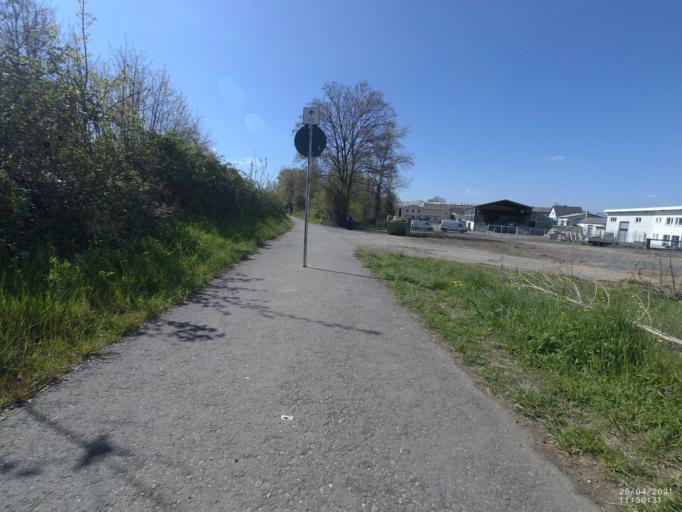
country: DE
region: Rheinland-Pfalz
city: Sankt Sebastian
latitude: 50.4269
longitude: 7.5692
